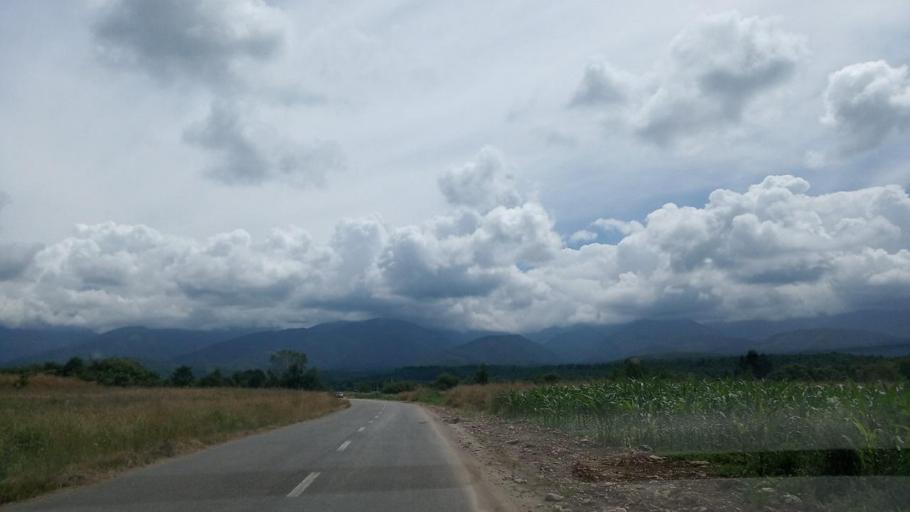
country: RO
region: Sibiu
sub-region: Comuna Porumbacu de Jos
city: Porumbacu de Jos
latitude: 45.7103
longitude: 24.4783
